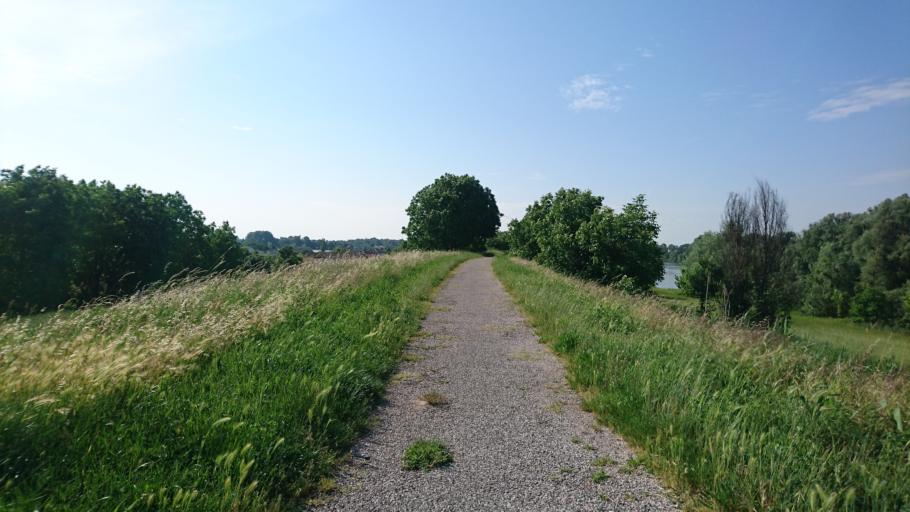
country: IT
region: Veneto
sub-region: Provincia di Verona
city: Villa Bartolomea
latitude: 45.1834
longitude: 11.3277
